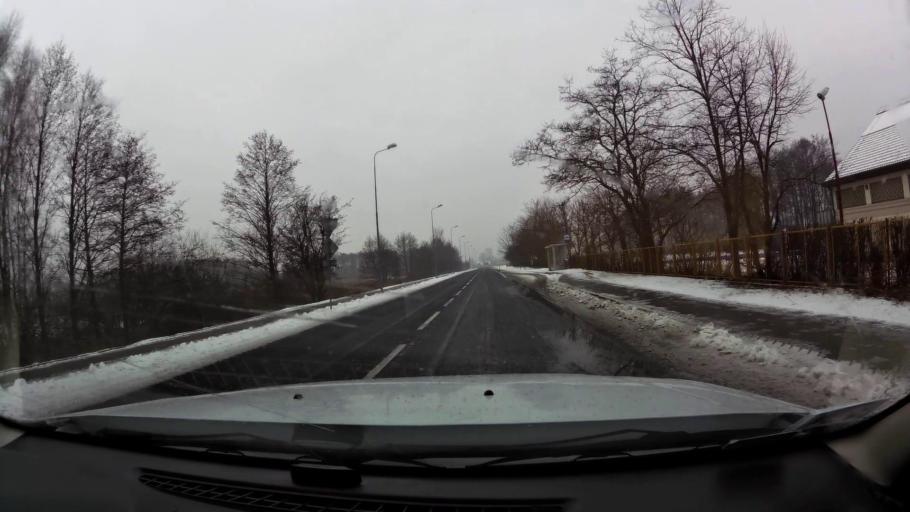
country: PL
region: West Pomeranian Voivodeship
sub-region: Powiat gryficki
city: Mrzezyno
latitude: 54.1404
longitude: 15.2872
